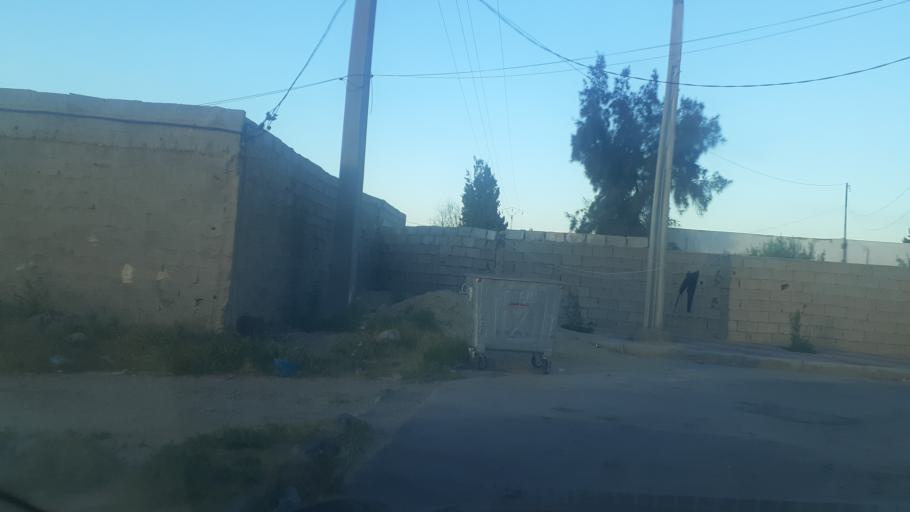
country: TN
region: Qabis
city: Gabes
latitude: 33.9327
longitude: 10.0406
